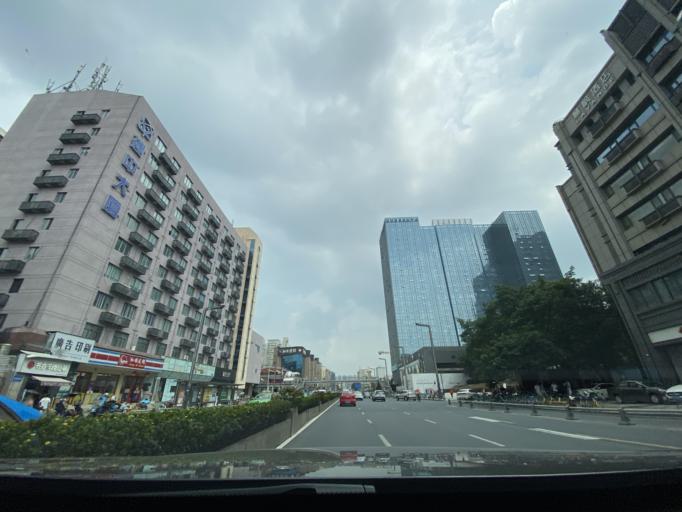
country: CN
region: Sichuan
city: Chengdu
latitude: 30.6311
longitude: 104.0740
